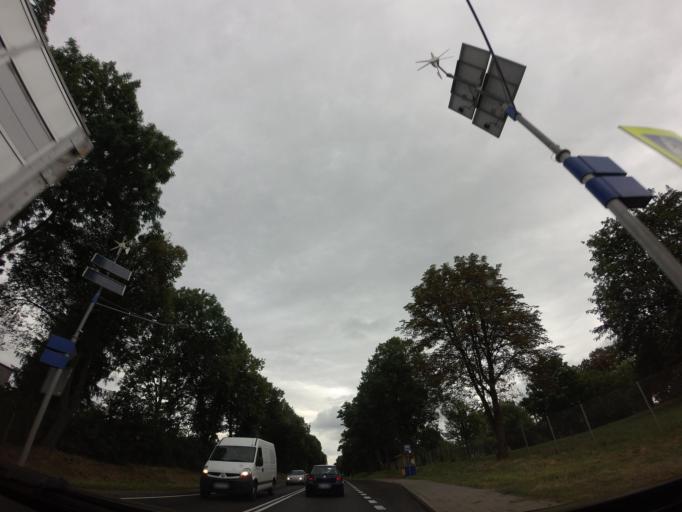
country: PL
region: Masovian Voivodeship
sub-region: Powiat ciechanowski
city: Ciechanow
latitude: 52.8624
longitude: 20.5706
